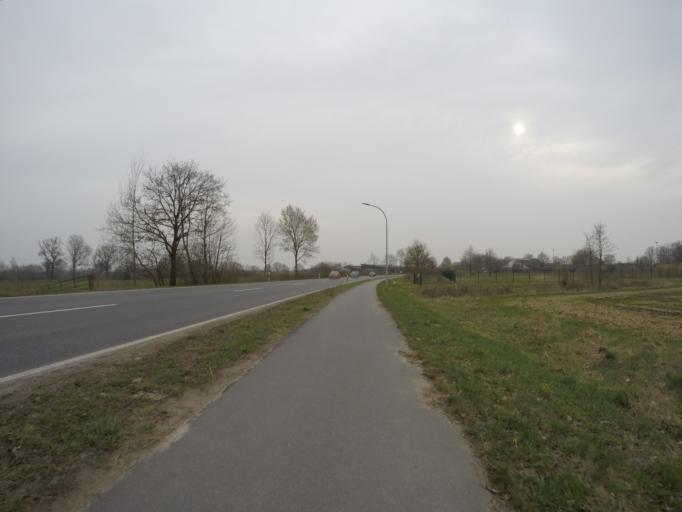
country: DE
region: Schleswig-Holstein
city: Borstel-Hohenraden
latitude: 53.6912
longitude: 9.8178
